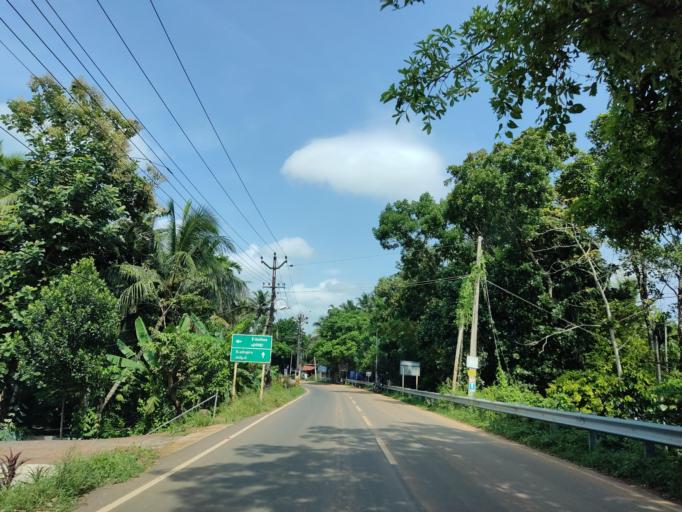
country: IN
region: Kerala
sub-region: Alappuzha
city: Mavelikara
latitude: 9.3302
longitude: 76.4661
